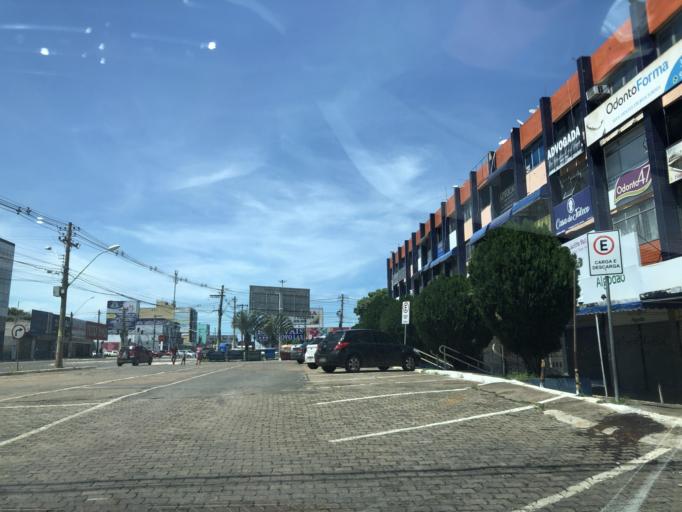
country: BR
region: Federal District
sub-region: Brasilia
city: Brasilia
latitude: -15.8021
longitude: -48.0682
